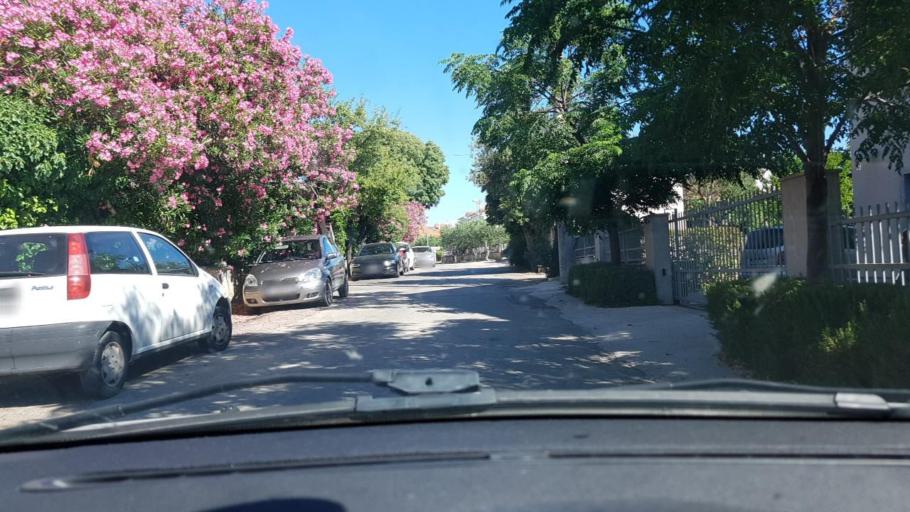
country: HR
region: Sibensko-Kniniska
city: Vodice
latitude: 43.7594
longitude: 15.7807
